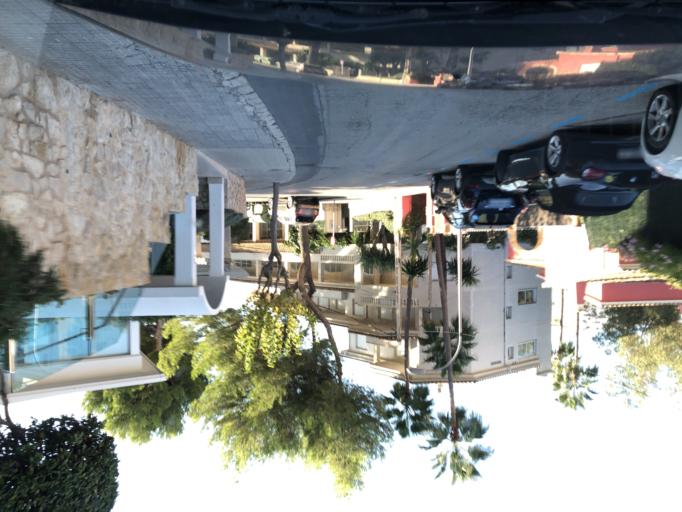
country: ES
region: Balearic Islands
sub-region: Illes Balears
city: Camp de Mar
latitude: 39.5392
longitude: 2.4499
